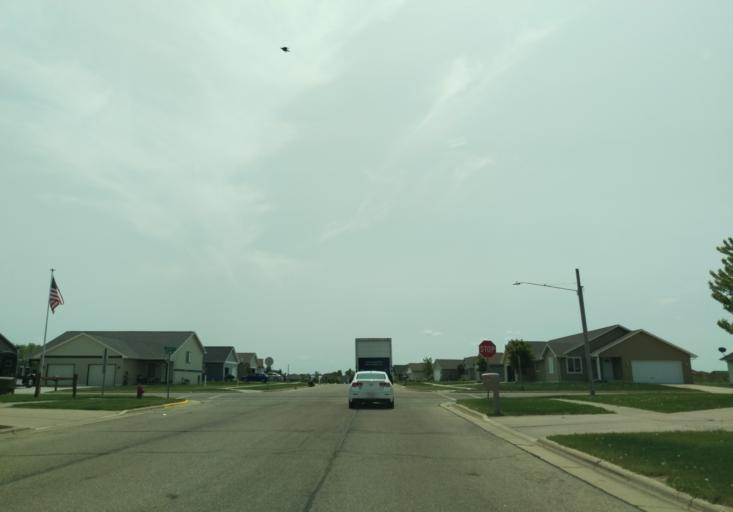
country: US
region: Wisconsin
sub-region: Rock County
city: Evansville
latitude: 42.7771
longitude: -89.3169
